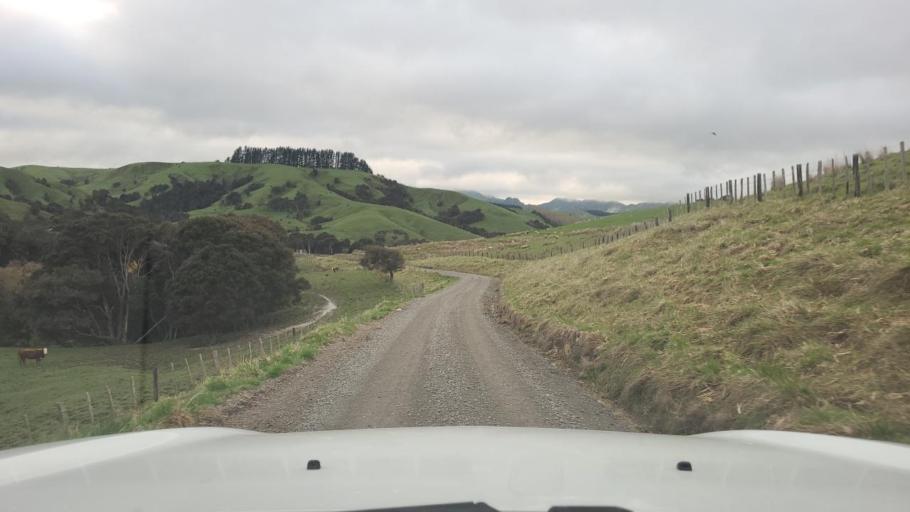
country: NZ
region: Wellington
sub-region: Masterton District
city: Masterton
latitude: -41.1663
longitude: 175.6960
